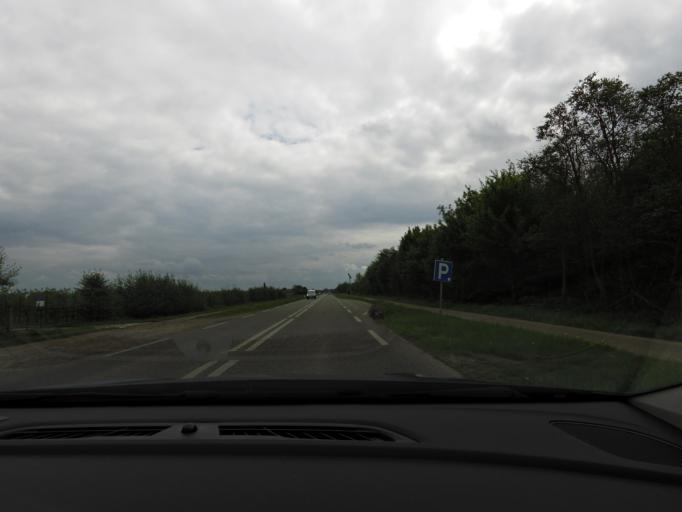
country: NL
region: Gelderland
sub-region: Gemeente Tiel
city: Tiel
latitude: 51.9019
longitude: 5.3698
